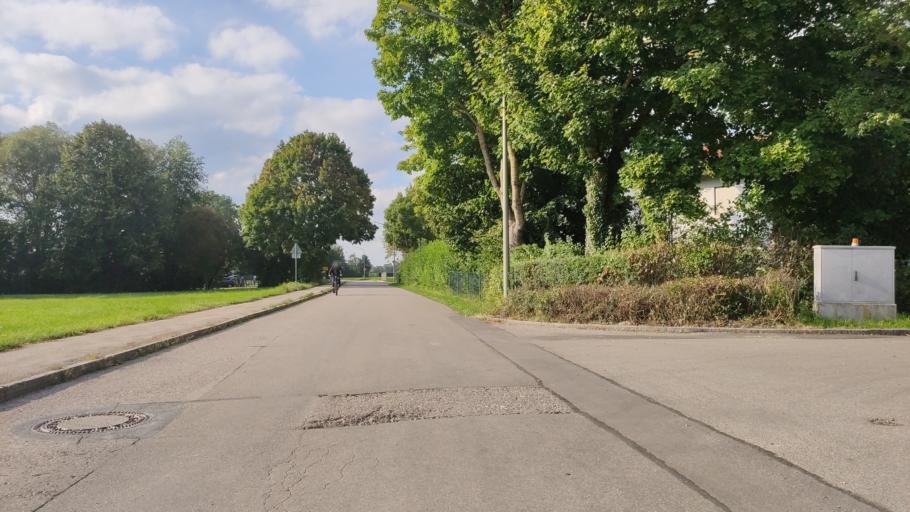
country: DE
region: Bavaria
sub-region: Upper Bavaria
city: Prittriching
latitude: 48.2062
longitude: 10.9247
